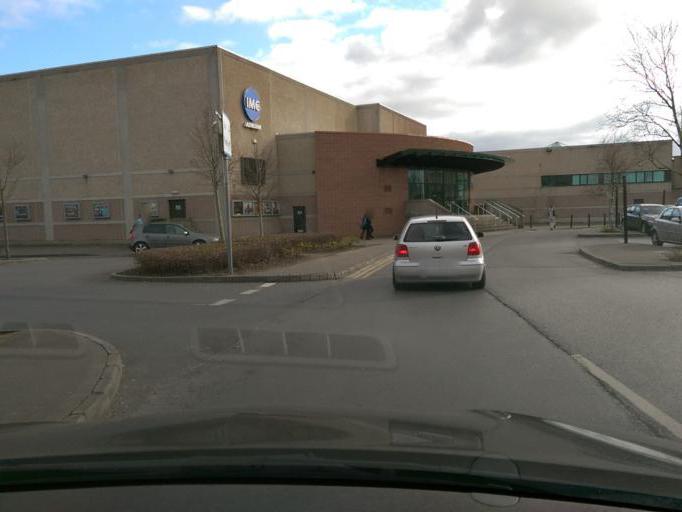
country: IE
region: Leinster
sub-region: An Iarmhi
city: Athlone
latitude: 53.4209
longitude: -7.9332
